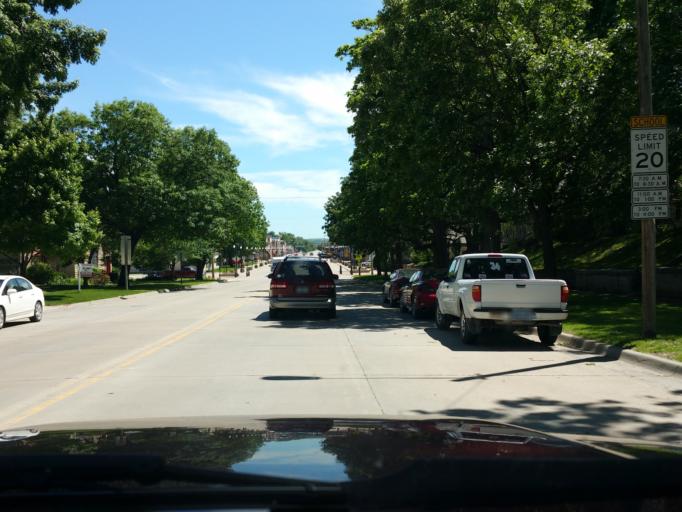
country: US
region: Kansas
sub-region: Pottawatomie County
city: Wamego
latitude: 39.2056
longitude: -96.3051
